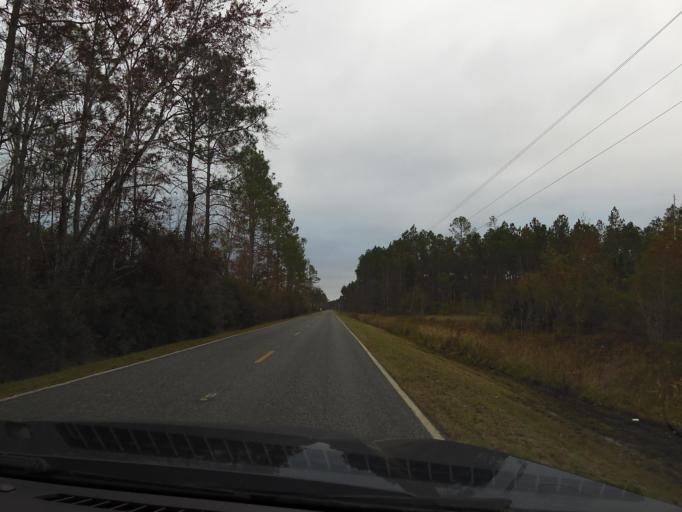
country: US
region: Georgia
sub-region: Charlton County
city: Folkston
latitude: 30.8745
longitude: -82.0472
